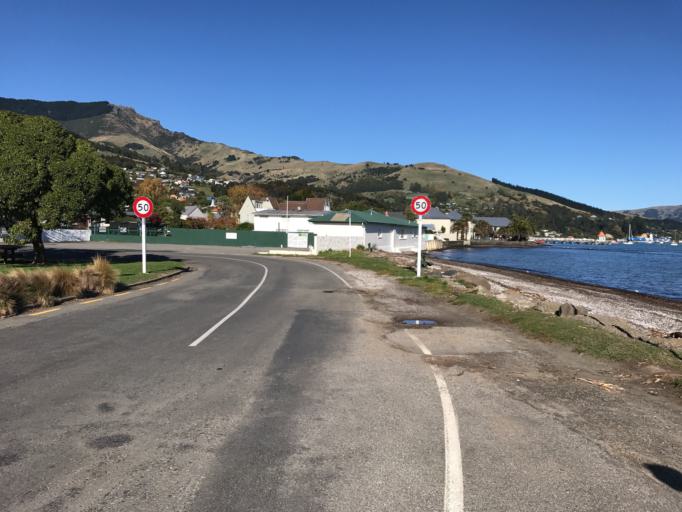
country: NZ
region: Canterbury
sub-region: Christchurch City
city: Christchurch
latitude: -43.8023
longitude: 172.9675
